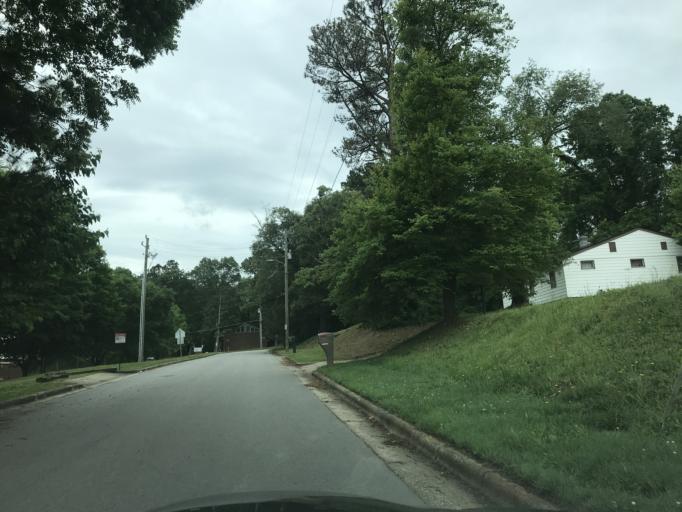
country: US
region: North Carolina
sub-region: Wake County
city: West Raleigh
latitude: 35.7910
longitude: -78.6885
